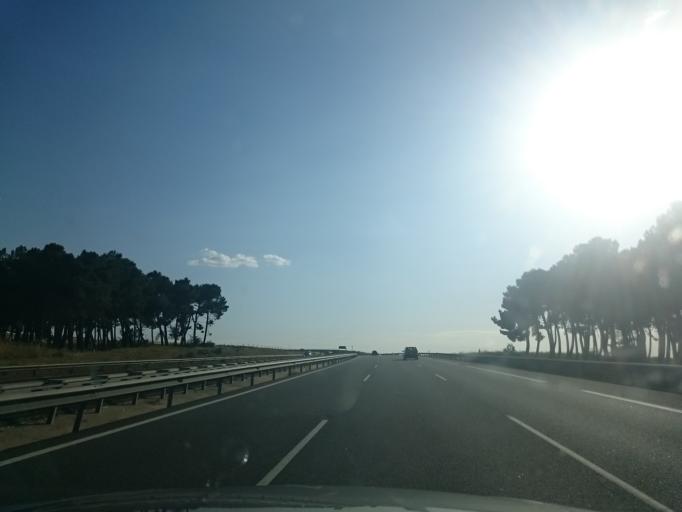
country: ES
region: Castille and Leon
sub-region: Provincia de Burgos
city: Cardenajimeno
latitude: 42.3298
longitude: -3.6502
